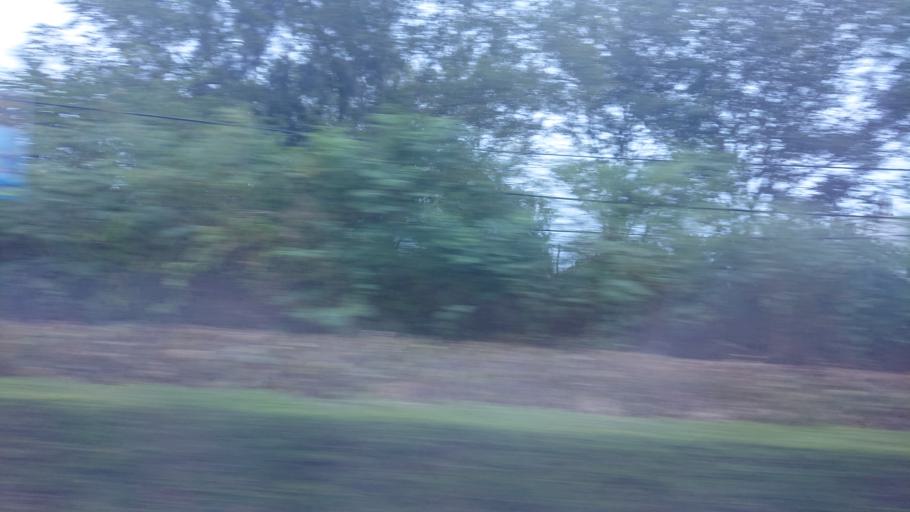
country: TW
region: Fukien
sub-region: Kinmen
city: Jincheng
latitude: 24.4123
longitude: 118.3014
